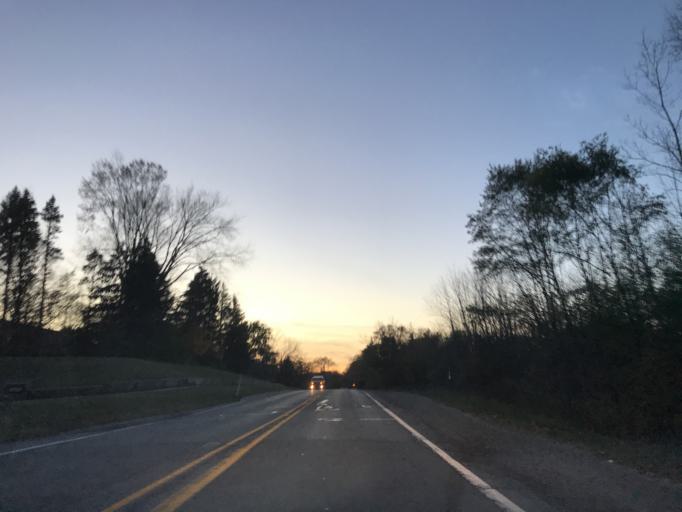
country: US
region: Michigan
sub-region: Oakland County
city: Farmington Hills
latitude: 42.4846
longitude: -83.3625
